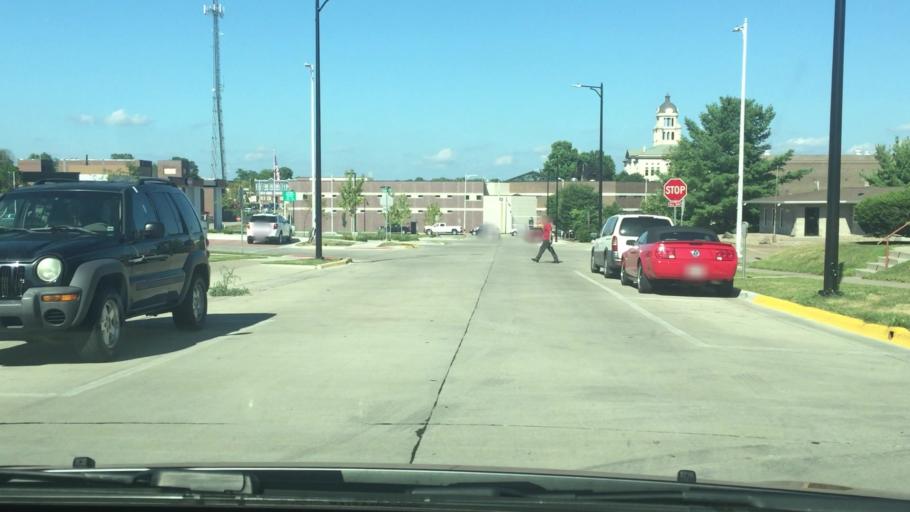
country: US
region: Iowa
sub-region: Muscatine County
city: Muscatine
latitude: 41.4232
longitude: -91.0466
